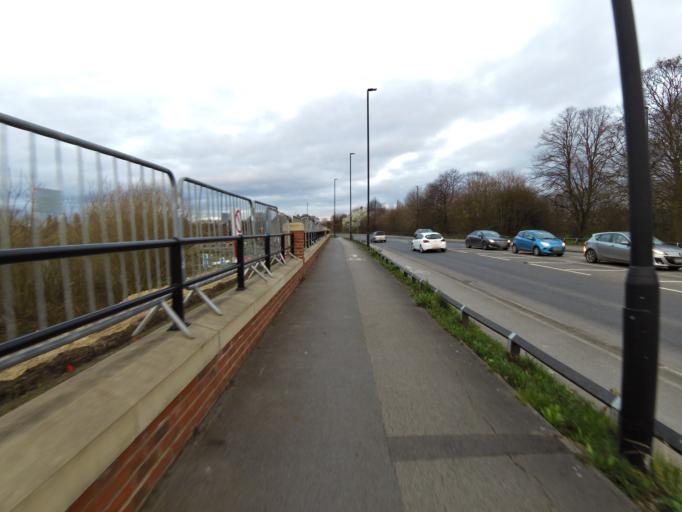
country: GB
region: England
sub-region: City of York
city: York
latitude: 53.9657
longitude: -1.1088
